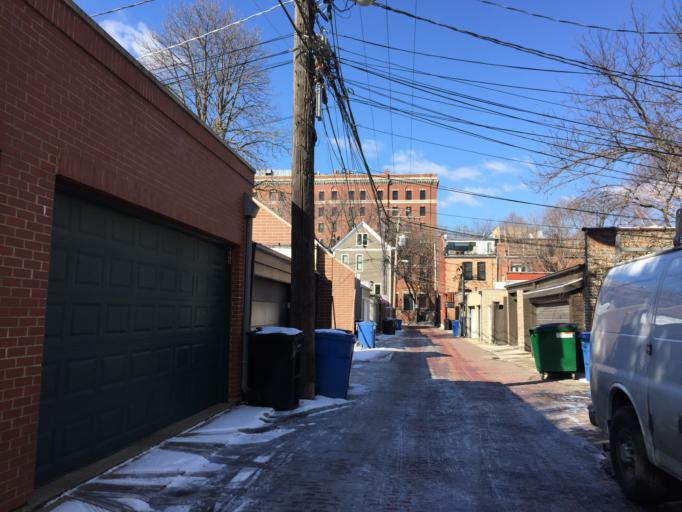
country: US
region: Illinois
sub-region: Cook County
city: Chicago
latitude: 41.9262
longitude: -87.6451
